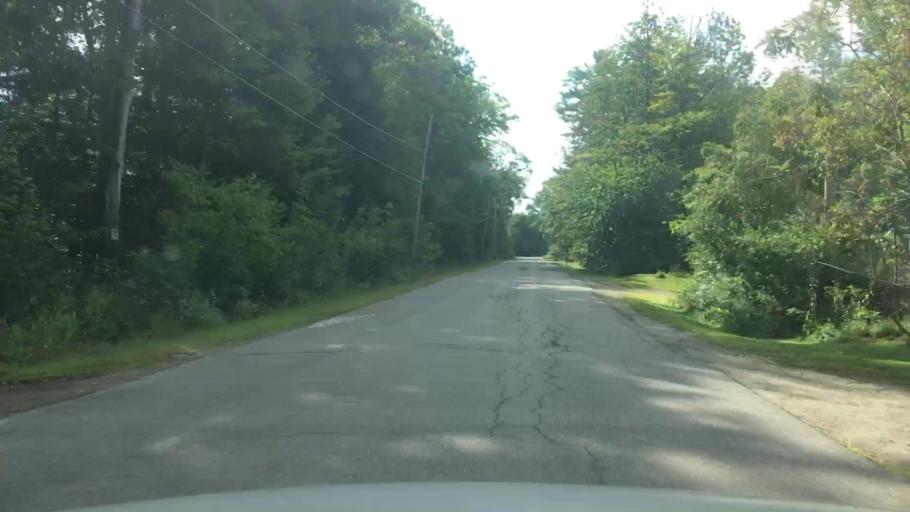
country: US
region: Maine
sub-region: Kennebec County
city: Gardiner
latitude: 44.1727
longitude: -69.8186
